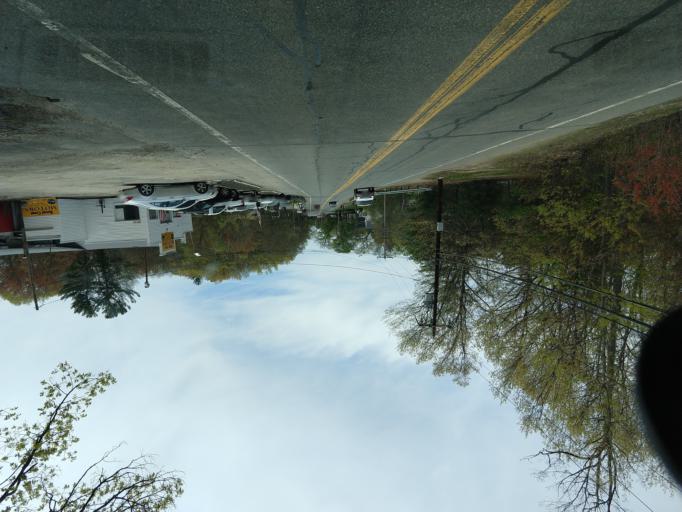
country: US
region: Massachusetts
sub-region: Essex County
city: Merrimac
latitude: 42.8112
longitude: -71.0331
